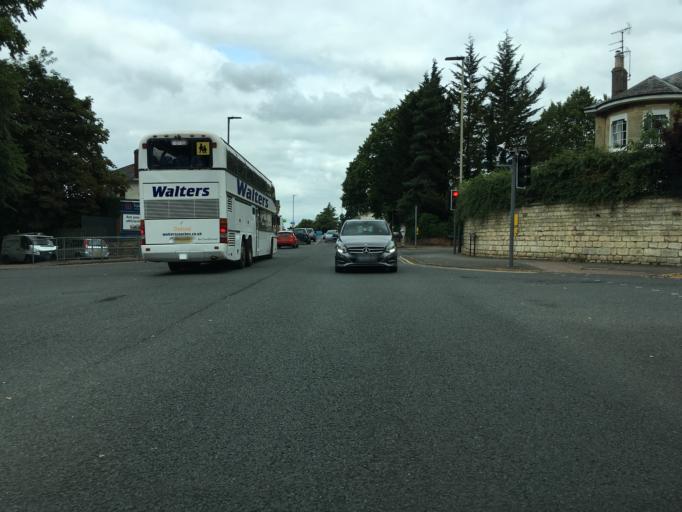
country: GB
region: England
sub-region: Gloucestershire
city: Charlton Kings
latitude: 51.8879
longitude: -2.0522
